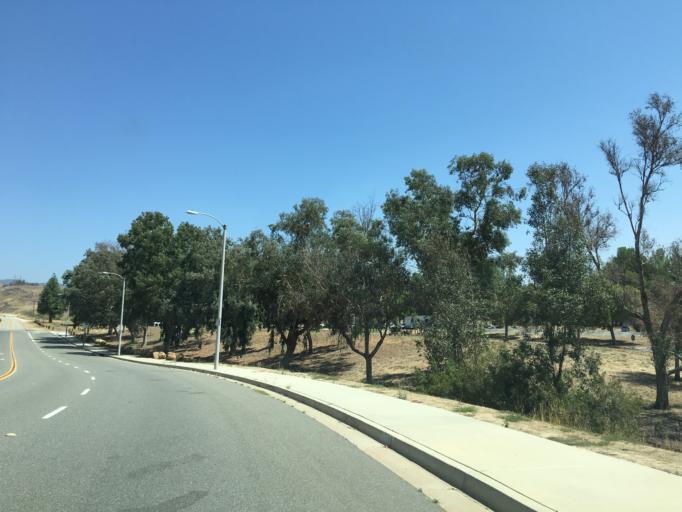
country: US
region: California
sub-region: Los Angeles County
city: Castaic
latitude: 34.5026
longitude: -118.6160
